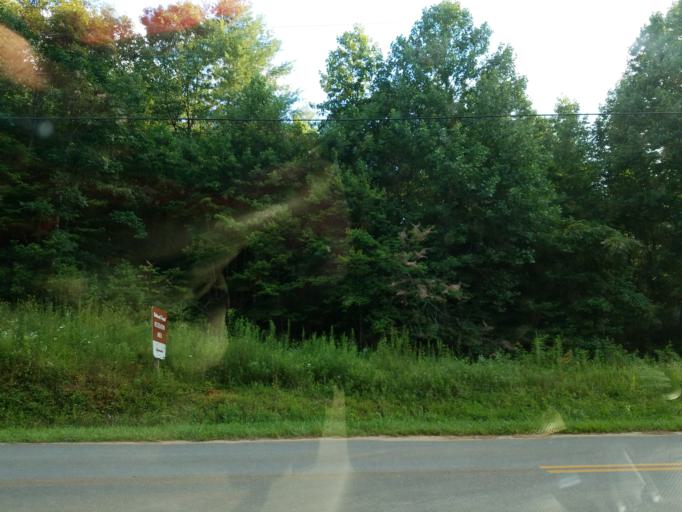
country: US
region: Georgia
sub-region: Union County
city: Blairsville
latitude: 34.7396
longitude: -84.0679
